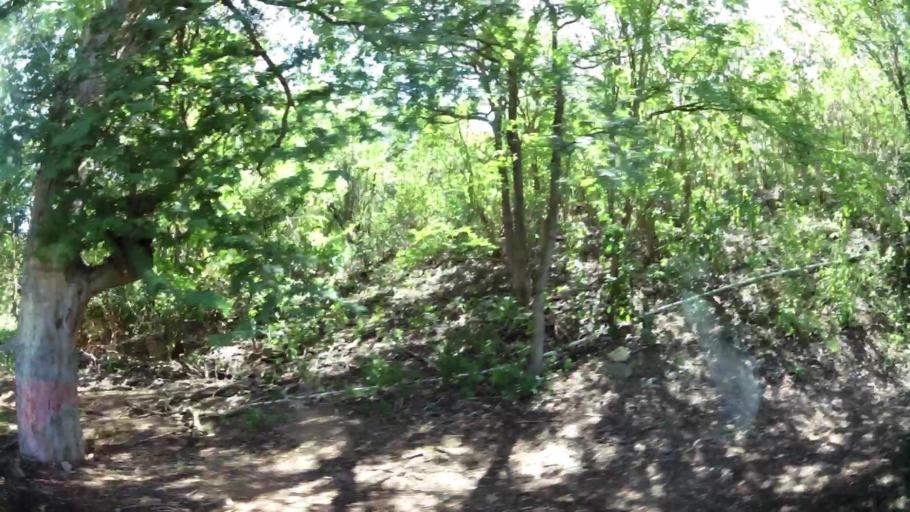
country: AG
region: Saint Paul
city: Falmouth
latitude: 17.0072
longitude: -61.7577
